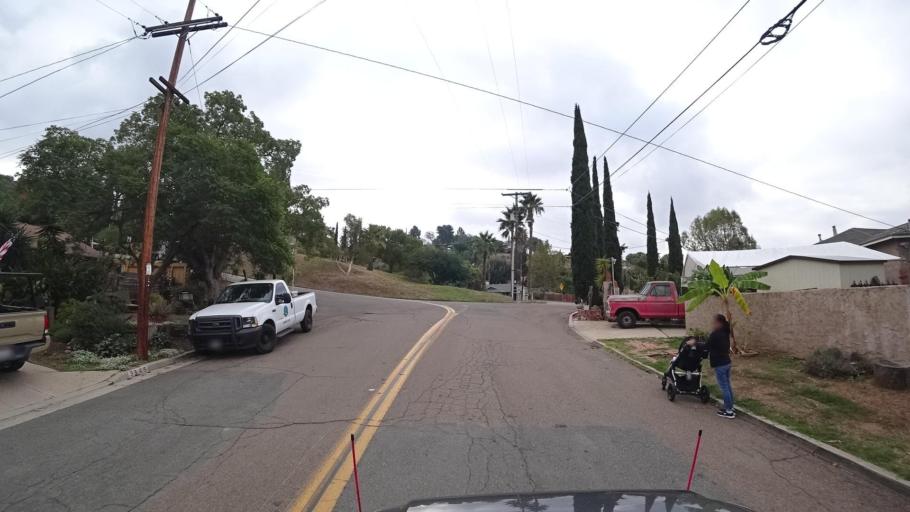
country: US
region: California
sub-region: San Diego County
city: Spring Valley
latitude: 32.7473
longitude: -117.0119
